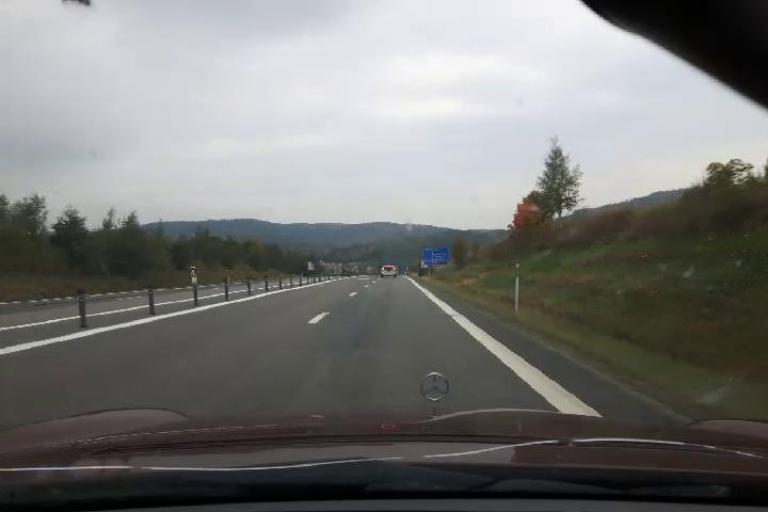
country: SE
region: Vaesternorrland
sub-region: Kramfors Kommun
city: Nordingra
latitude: 63.0579
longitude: 18.3406
